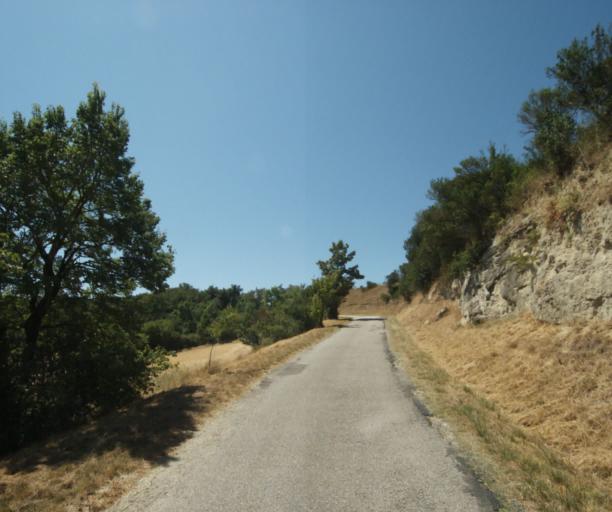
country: FR
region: Midi-Pyrenees
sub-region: Departement de la Haute-Garonne
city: Saint-Felix-Lauragais
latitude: 43.4753
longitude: 1.9185
